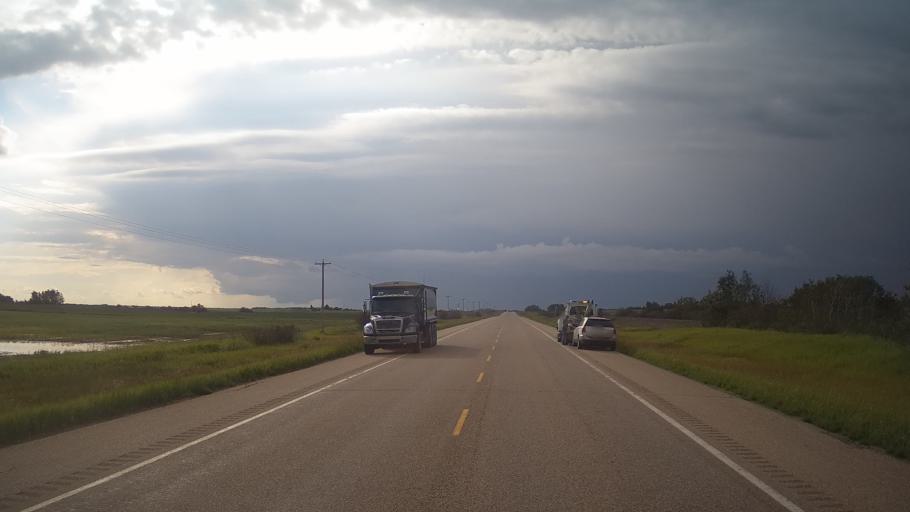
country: CA
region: Alberta
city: Vegreville
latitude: 53.2155
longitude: -112.1874
